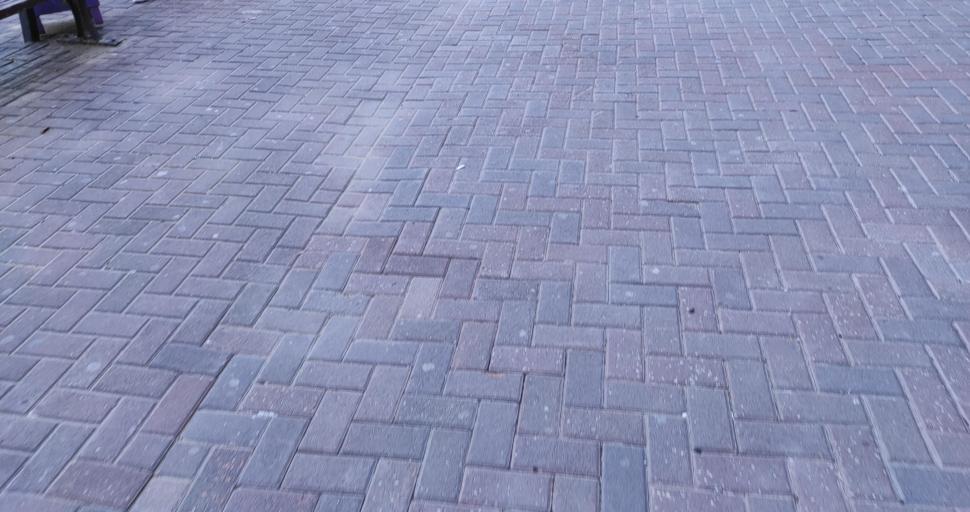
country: IL
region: Central District
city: Netanya
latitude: 32.3260
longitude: 34.8573
